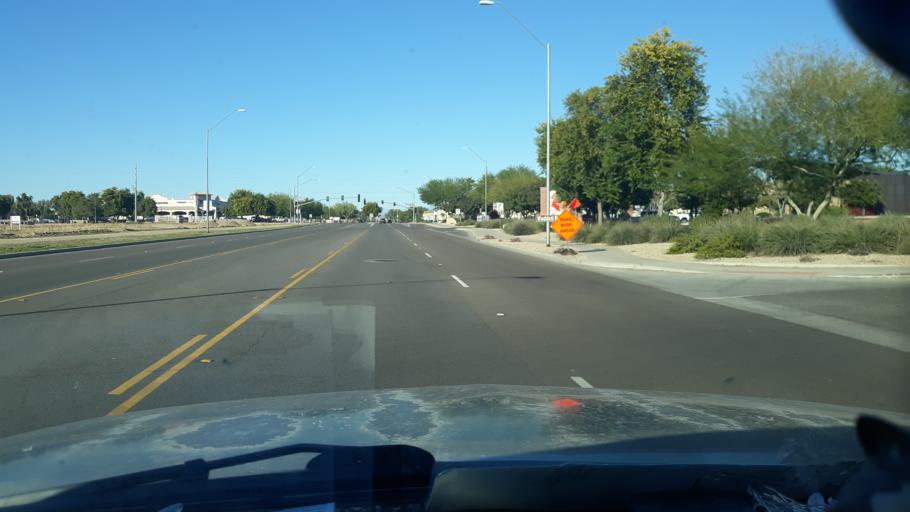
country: US
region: Arizona
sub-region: Maricopa County
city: Surprise
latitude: 33.6077
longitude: -112.3938
